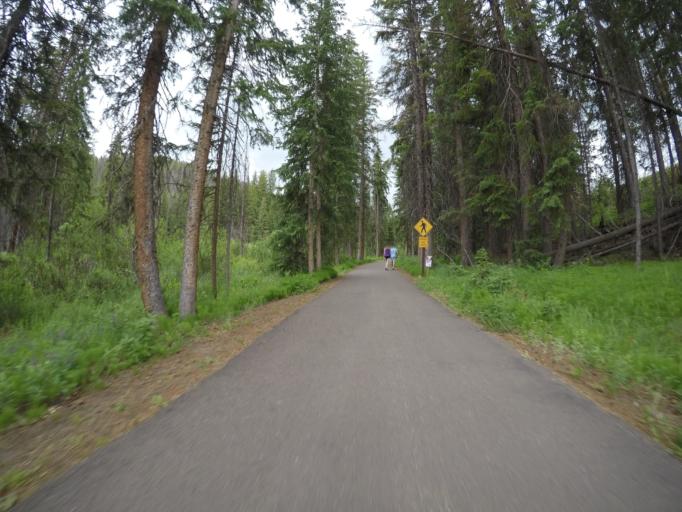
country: US
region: Colorado
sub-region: Grand County
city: Fraser
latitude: 39.9082
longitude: -105.7806
